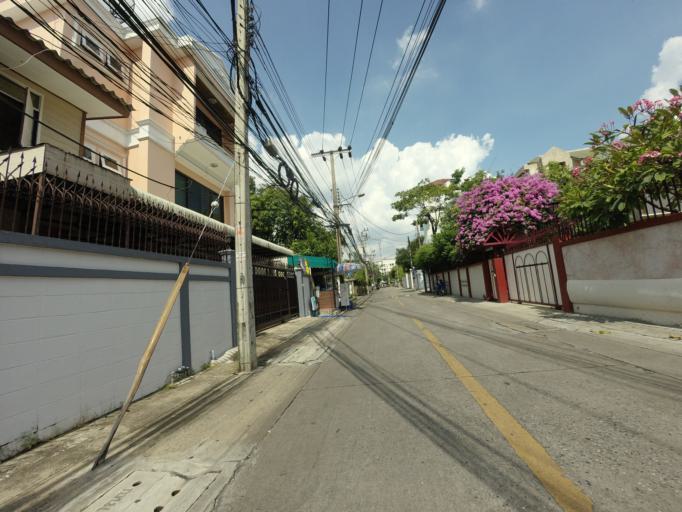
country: TH
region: Bangkok
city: Phaya Thai
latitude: 13.7822
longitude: 100.5518
